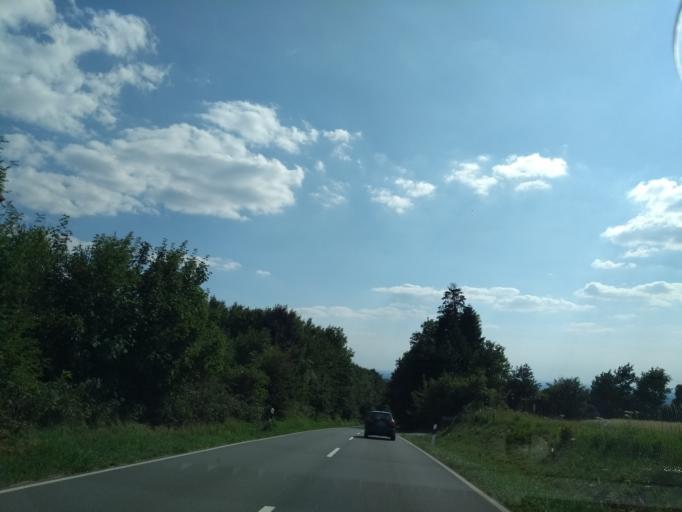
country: DE
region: North Rhine-Westphalia
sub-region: Regierungsbezirk Detmold
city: Altenbeken
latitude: 51.8149
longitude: 8.9085
